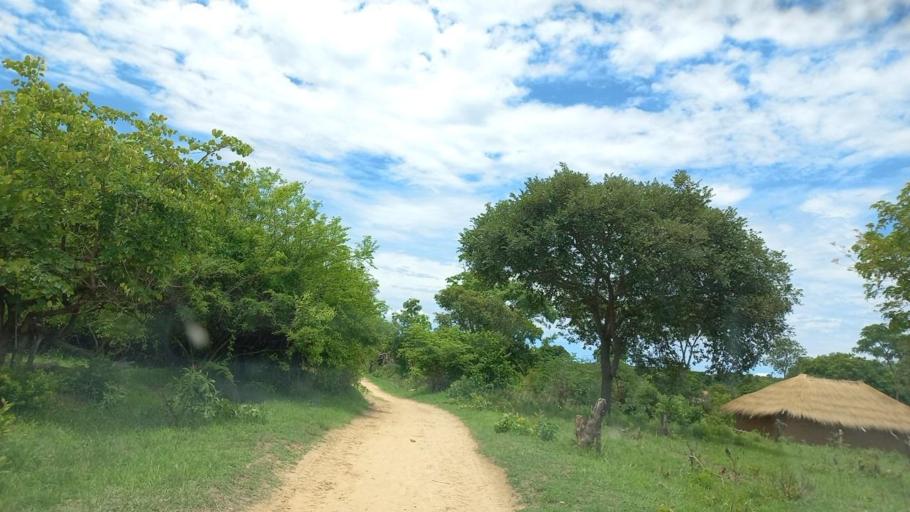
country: ZM
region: North-Western
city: Kabompo
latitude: -13.6223
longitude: 24.1902
